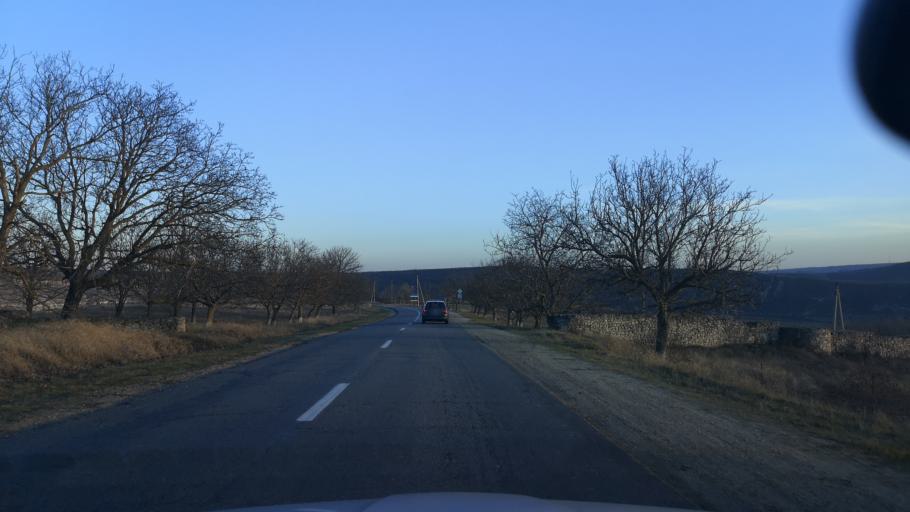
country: MD
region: Telenesti
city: Cocieri
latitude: 47.3099
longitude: 28.9722
